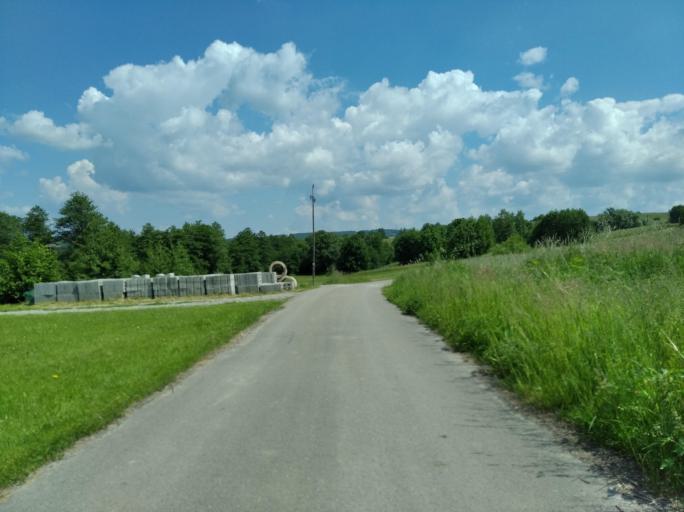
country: PL
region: Subcarpathian Voivodeship
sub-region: Powiat strzyzowski
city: Jawornik
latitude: 49.7891
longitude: 21.8655
